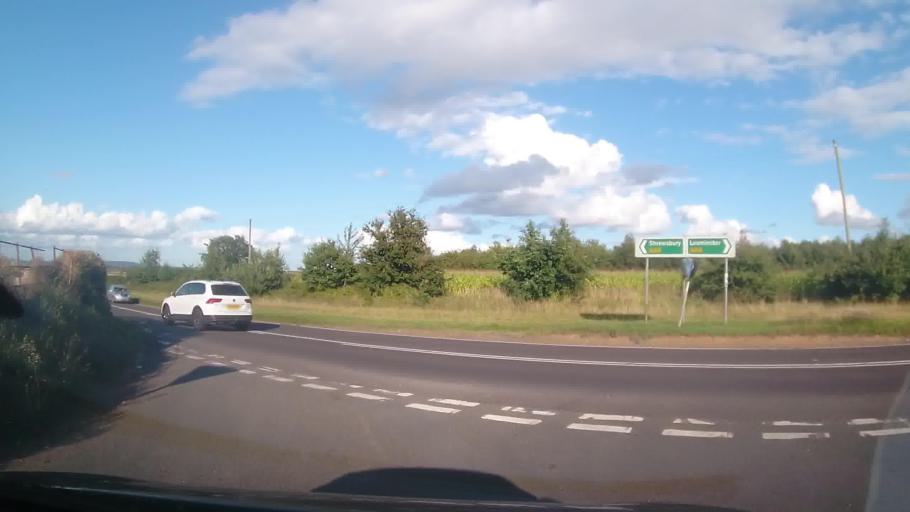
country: GB
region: England
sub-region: Shropshire
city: Bayston Hill
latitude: 52.6521
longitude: -2.7706
